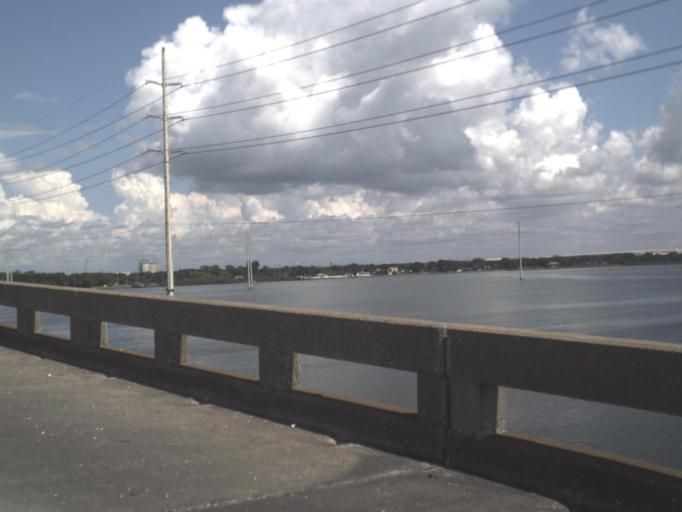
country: US
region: Florida
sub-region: Hillsborough County
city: Tampa
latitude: 27.9323
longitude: -82.4295
